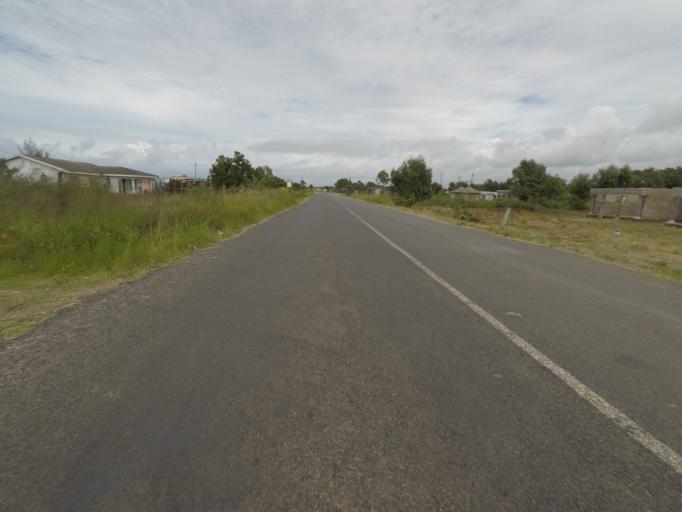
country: ZA
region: KwaZulu-Natal
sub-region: uThungulu District Municipality
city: eSikhawini
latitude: -28.9056
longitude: 31.8844
